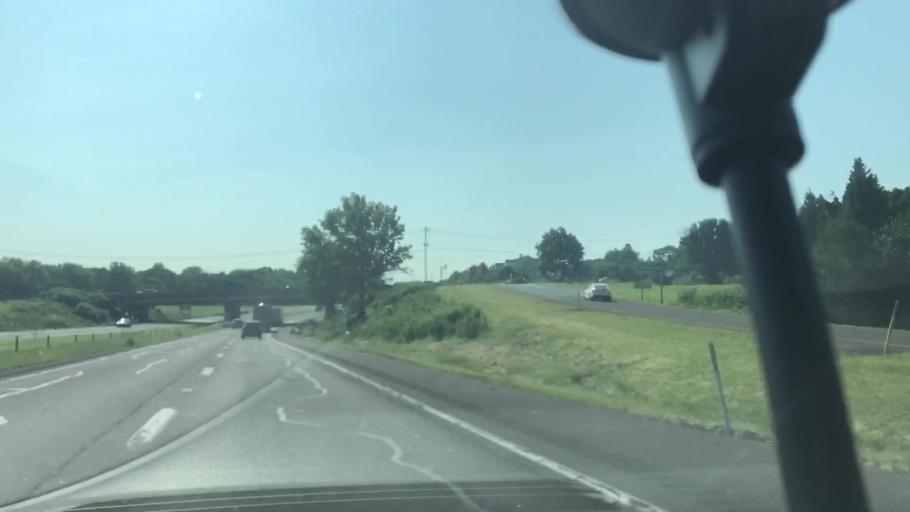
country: US
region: Pennsylvania
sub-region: Montgomery County
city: Royersford
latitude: 40.1964
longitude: -75.5271
